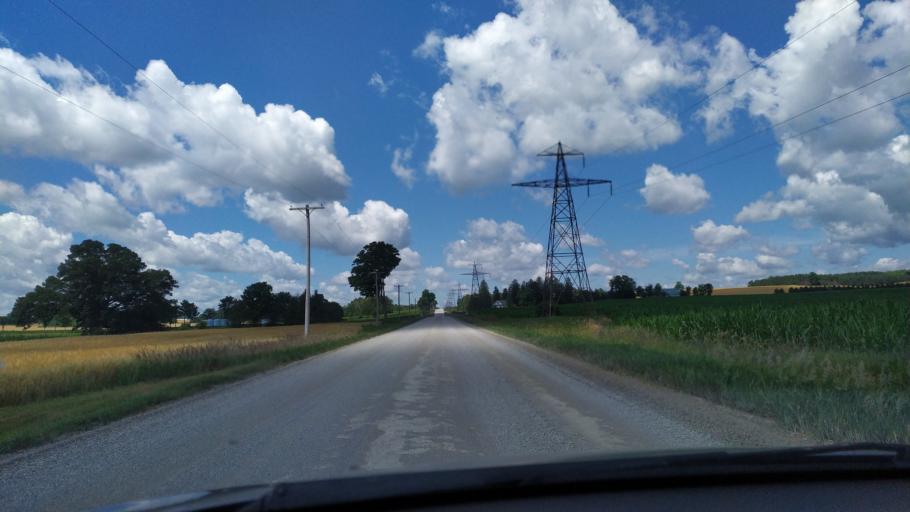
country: CA
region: Ontario
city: Stratford
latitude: 43.3874
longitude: -80.7751
